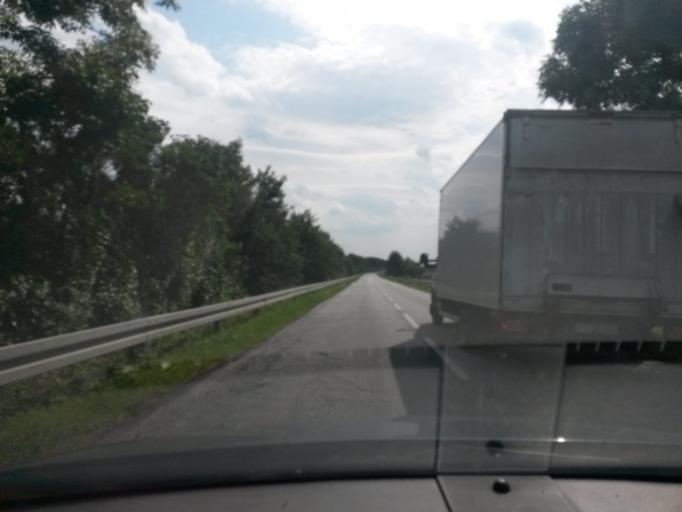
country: PL
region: Greater Poland Voivodeship
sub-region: Powiat poznanski
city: Kornik
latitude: 52.2933
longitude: 17.1204
